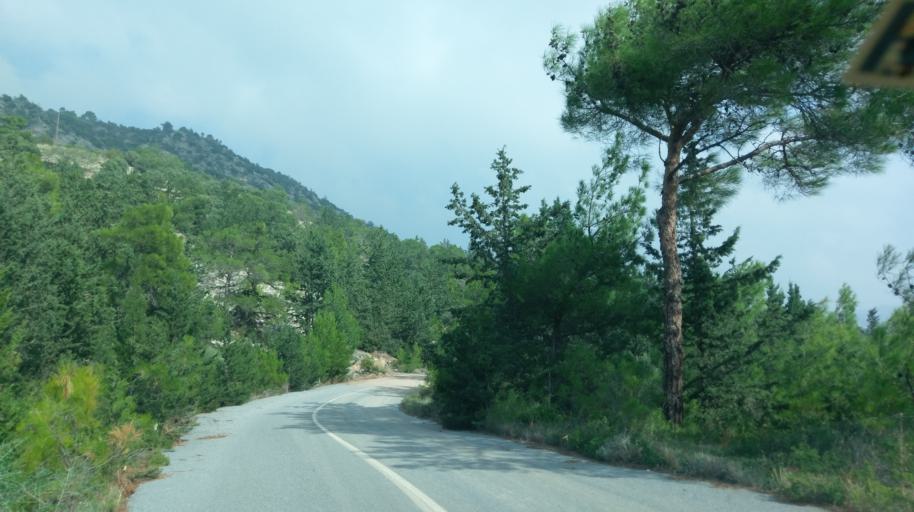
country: CY
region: Ammochostos
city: Lefkonoiko
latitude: 35.3151
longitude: 33.6172
